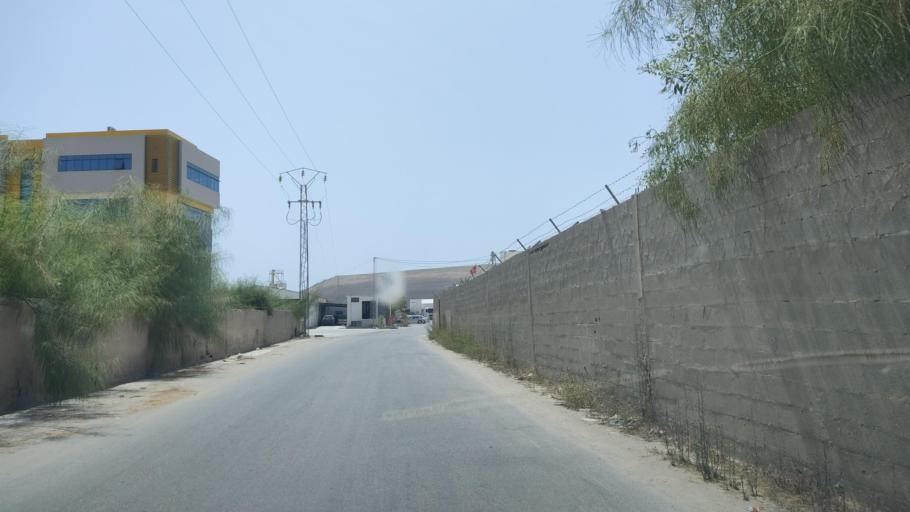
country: TN
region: Safaqis
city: Sfax
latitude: 34.7057
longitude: 10.7248
